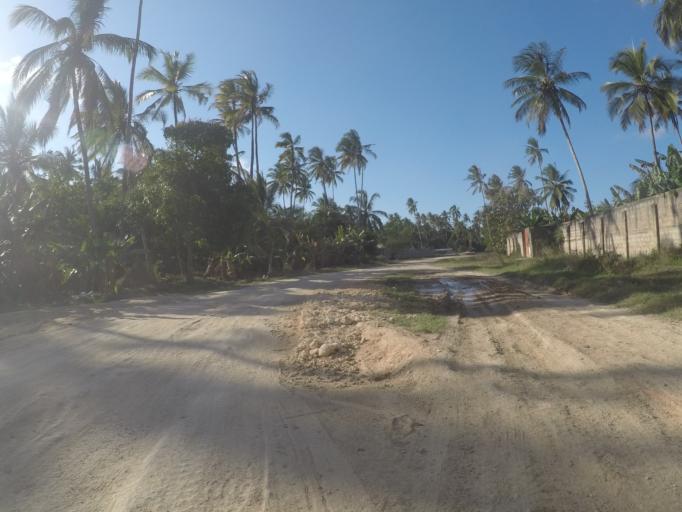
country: TZ
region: Zanzibar Central/South
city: Koani
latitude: -6.1656
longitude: 39.2867
